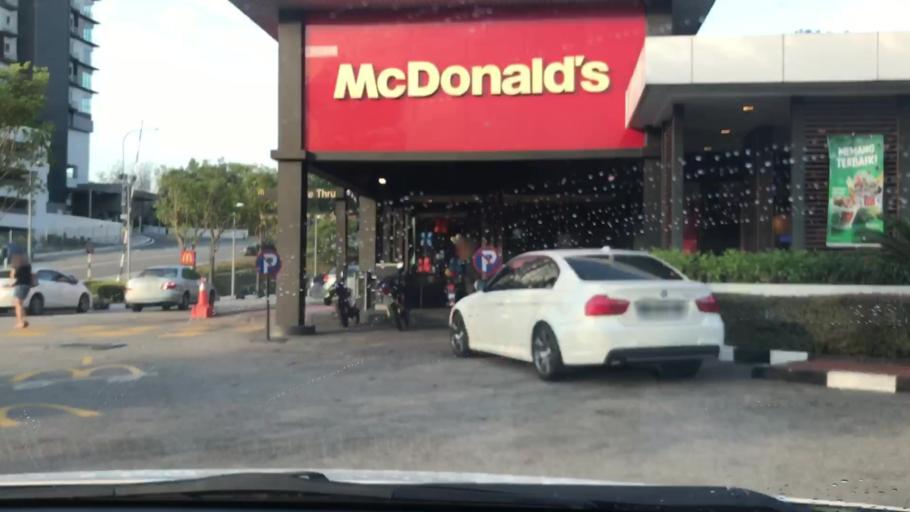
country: MY
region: Putrajaya
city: Putrajaya
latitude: 2.9957
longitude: 101.6707
